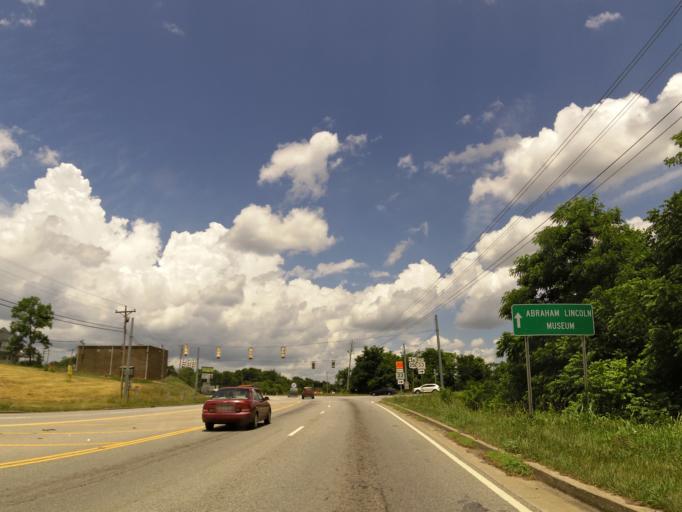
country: US
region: Tennessee
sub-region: Claiborne County
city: Tazewell
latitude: 36.4556
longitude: -83.5677
